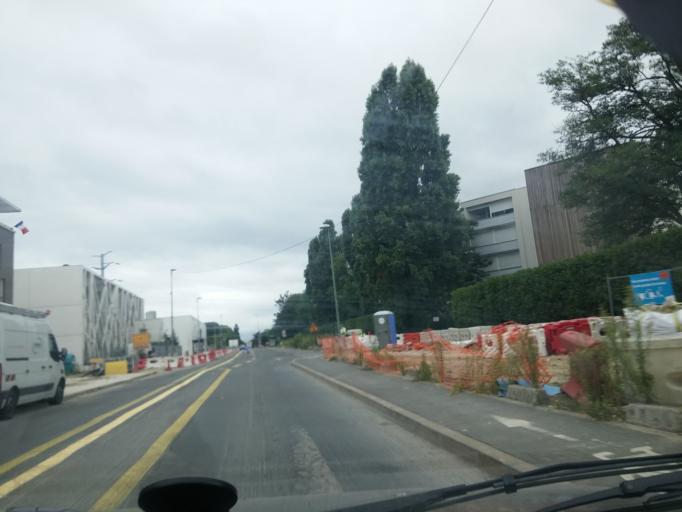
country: FR
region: Ile-de-France
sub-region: Departement du Val-de-Marne
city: Thiais
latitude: 48.7670
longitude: 2.3821
